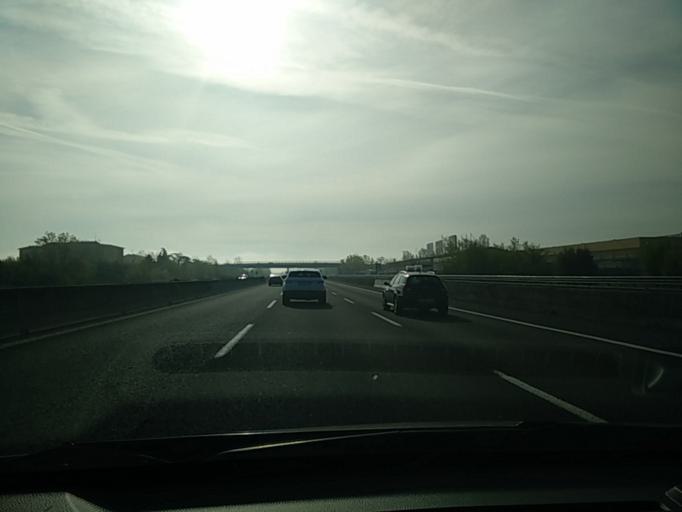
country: IT
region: Emilia-Romagna
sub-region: Provincia di Bologna
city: Ozzano dell'Emilia
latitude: 44.4622
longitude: 11.4994
